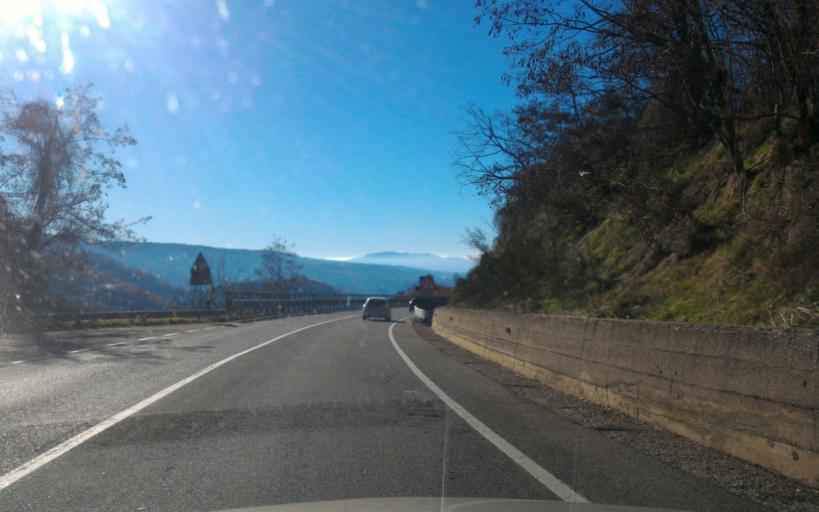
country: IT
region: Calabria
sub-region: Provincia di Cosenza
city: Spezzano della Sila
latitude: 39.2998
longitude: 16.3559
